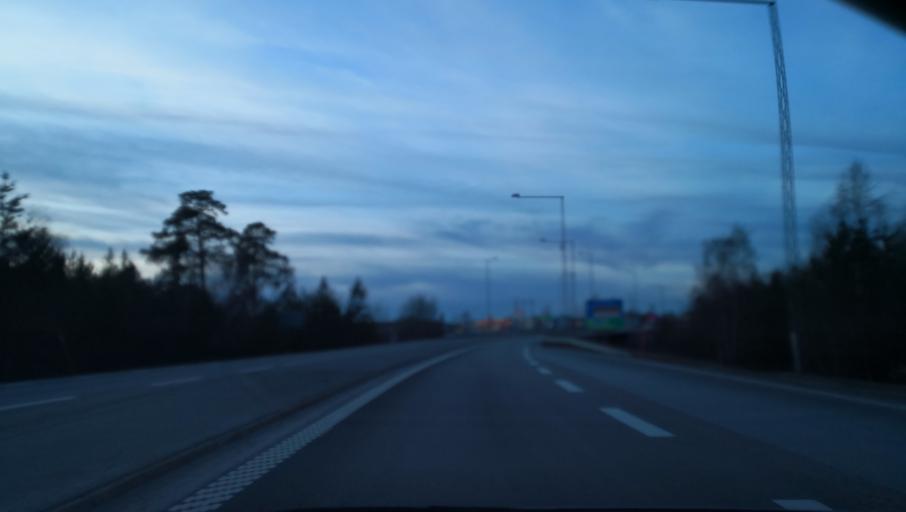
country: SE
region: Stockholm
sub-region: Varmdo Kommun
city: Gustavsberg
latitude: 59.3055
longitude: 18.3853
